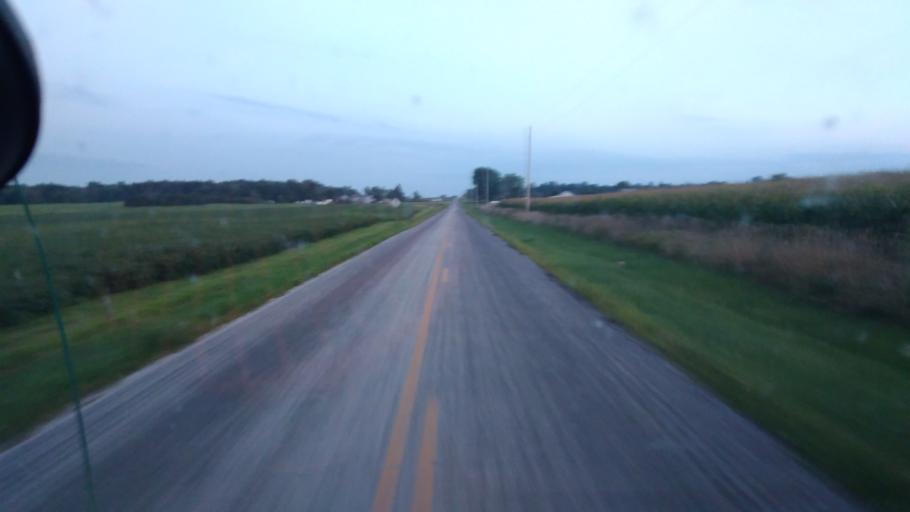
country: US
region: Ohio
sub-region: Hardin County
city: Kenton
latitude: 40.6425
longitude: -83.4579
